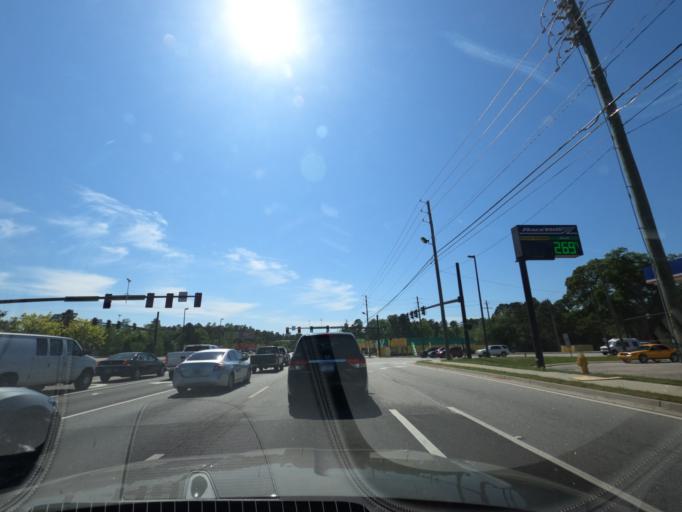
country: US
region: Georgia
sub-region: Columbia County
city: Martinez
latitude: 33.4662
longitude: -82.0854
